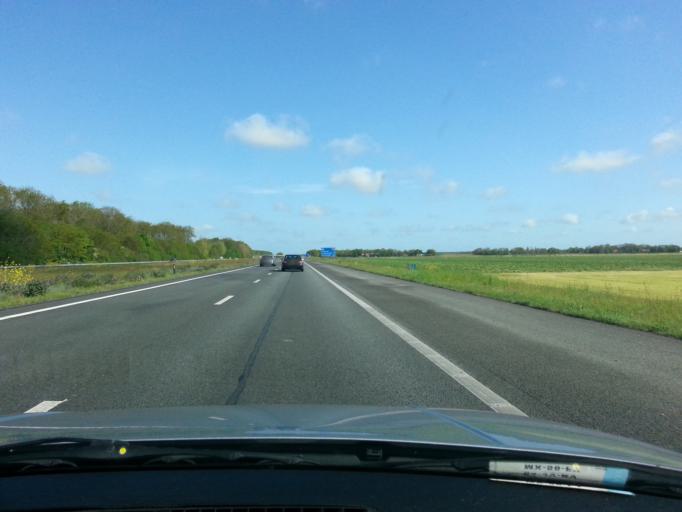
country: NL
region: Flevoland
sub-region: Gemeente Noordoostpolder
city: Emmeloord
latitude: 52.7533
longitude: 5.7685
